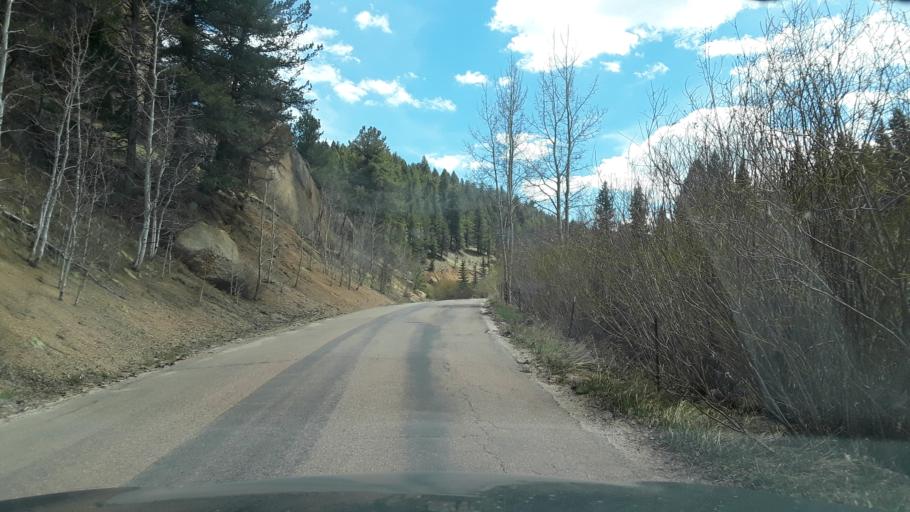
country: US
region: Colorado
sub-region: Teller County
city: Woodland Park
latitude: 39.0164
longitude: -105.0245
